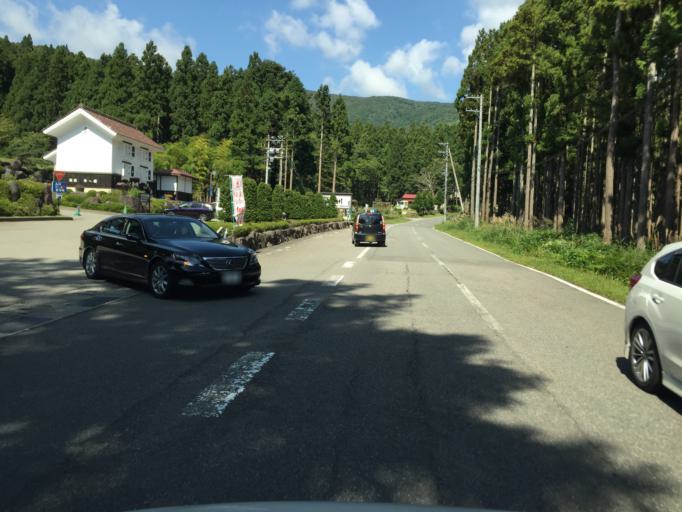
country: JP
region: Fukushima
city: Inawashiro
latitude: 37.5753
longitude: 140.0193
